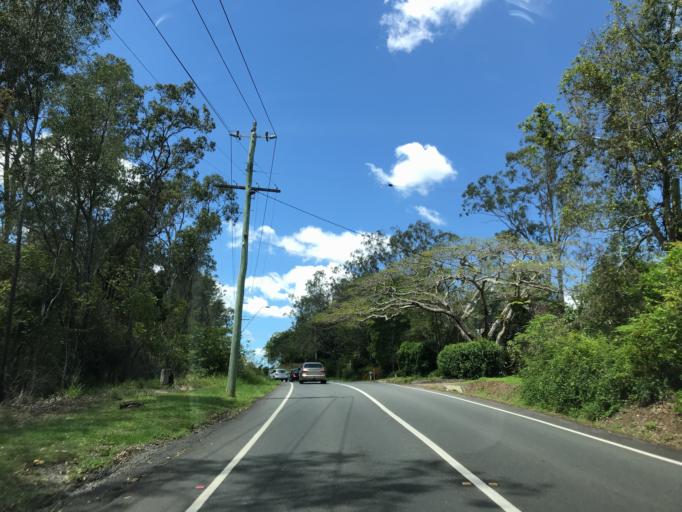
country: AU
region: Queensland
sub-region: Brisbane
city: Kenmore Hills
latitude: -27.4918
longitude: 152.9247
